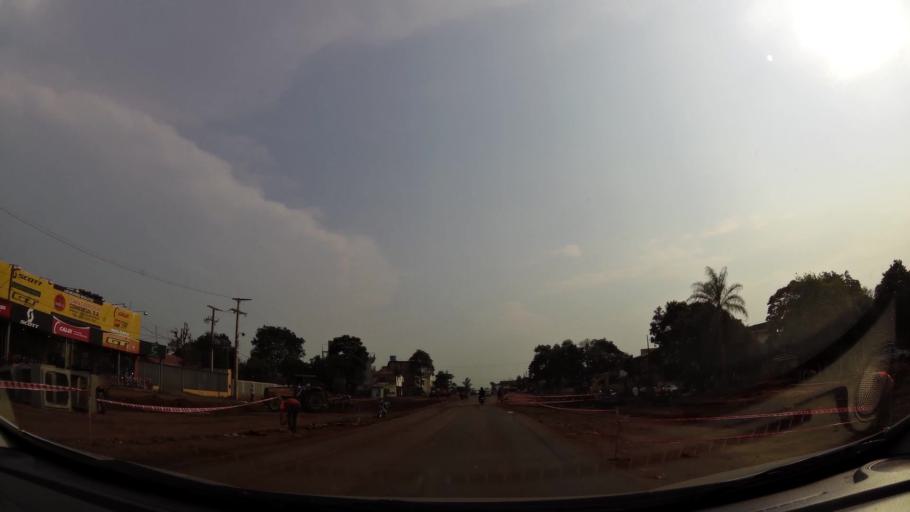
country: PY
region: Alto Parana
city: Ciudad del Este
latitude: -25.4819
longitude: -54.6583
